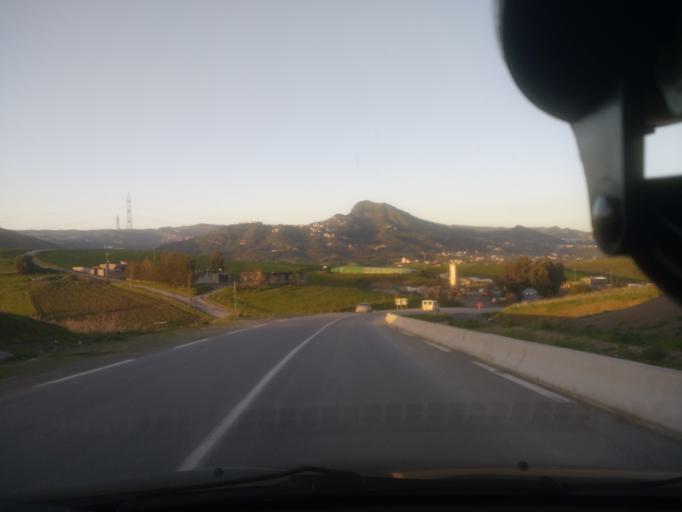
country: DZ
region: Boumerdes
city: Makouda
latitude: 36.7573
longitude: 4.0518
